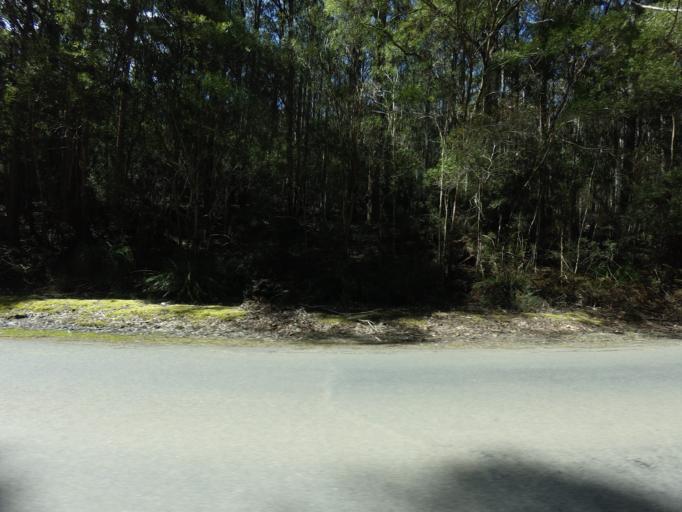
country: AU
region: Tasmania
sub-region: Derwent Valley
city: New Norfolk
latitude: -42.7349
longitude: 146.6654
